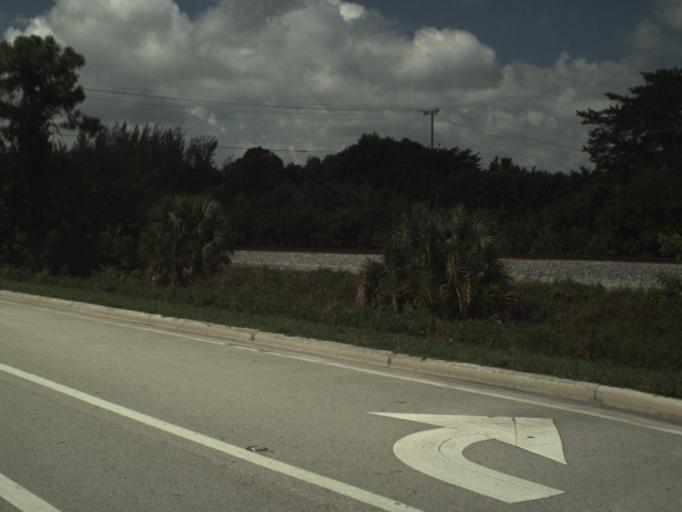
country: US
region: Florida
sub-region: Palm Beach County
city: Jupiter
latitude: 26.8984
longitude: -80.0948
